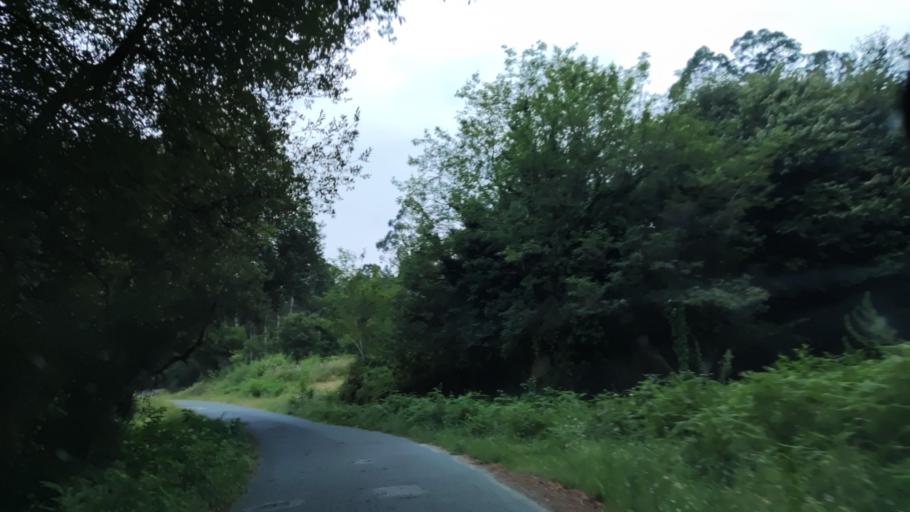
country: ES
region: Galicia
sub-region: Provincia de Pontevedra
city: Catoira
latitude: 42.6928
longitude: -8.7329
